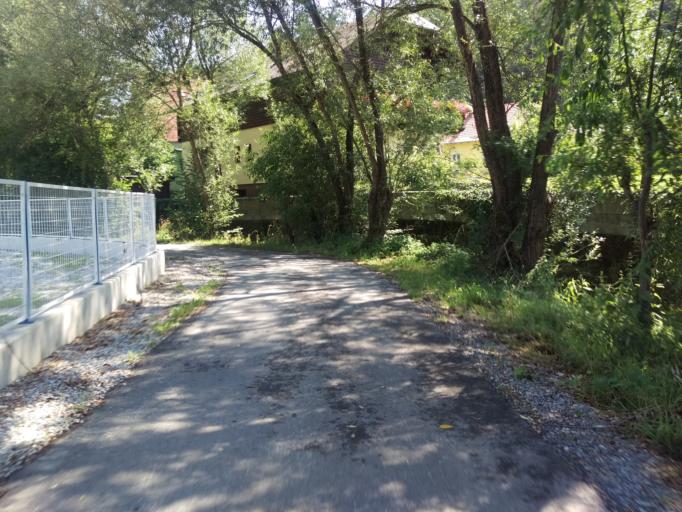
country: AT
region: Styria
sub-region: Politischer Bezirk Graz-Umgebung
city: Stattegg
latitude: 47.1262
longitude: 15.4434
